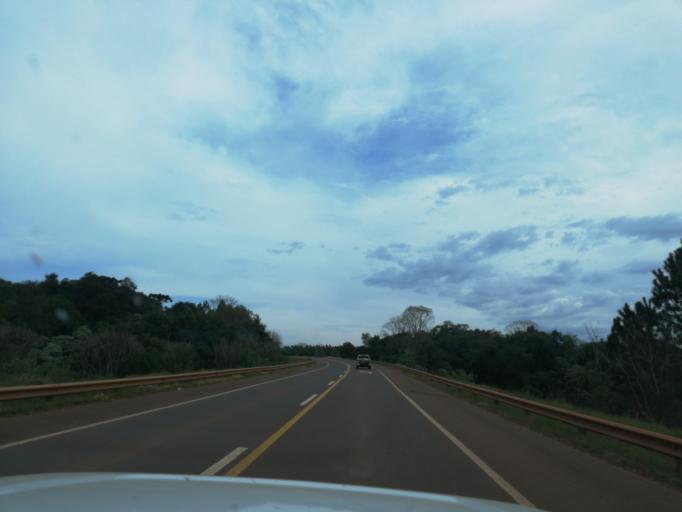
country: AR
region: Misiones
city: San Vicente
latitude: -26.6671
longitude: -54.1965
